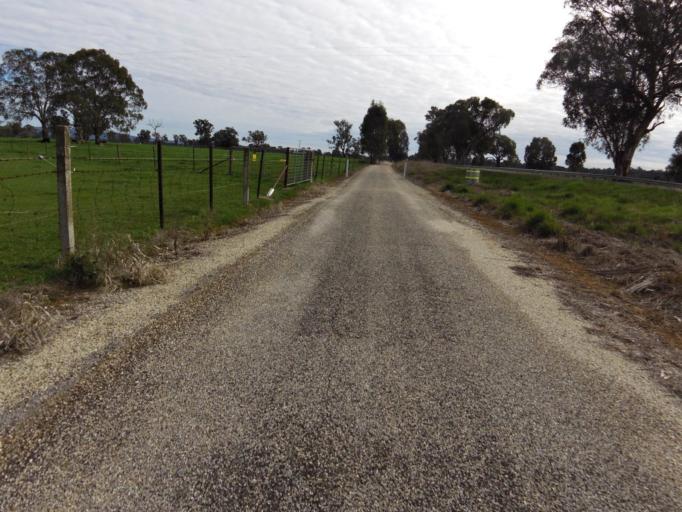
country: AU
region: Victoria
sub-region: Wangaratta
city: Wangaratta
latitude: -36.4197
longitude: 146.3564
